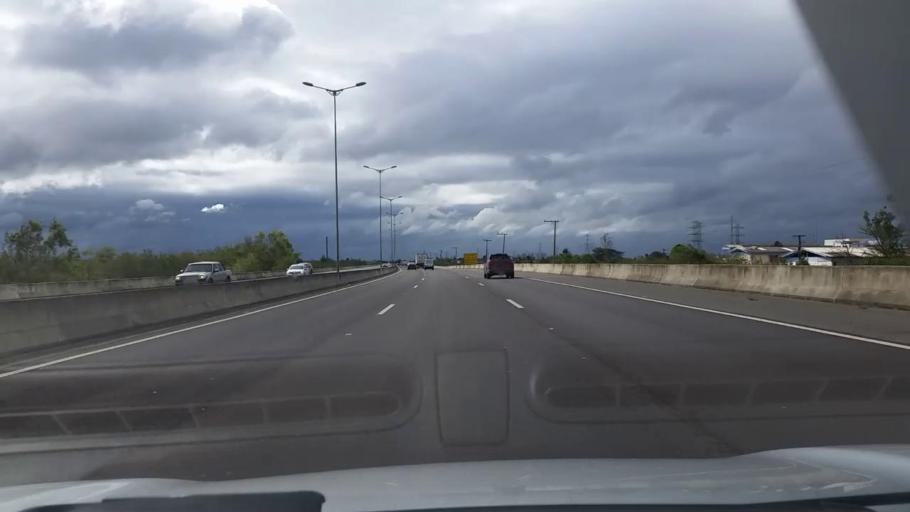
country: BR
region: Rio Grande do Sul
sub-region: Canoas
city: Canoas
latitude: -29.9558
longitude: -51.2024
